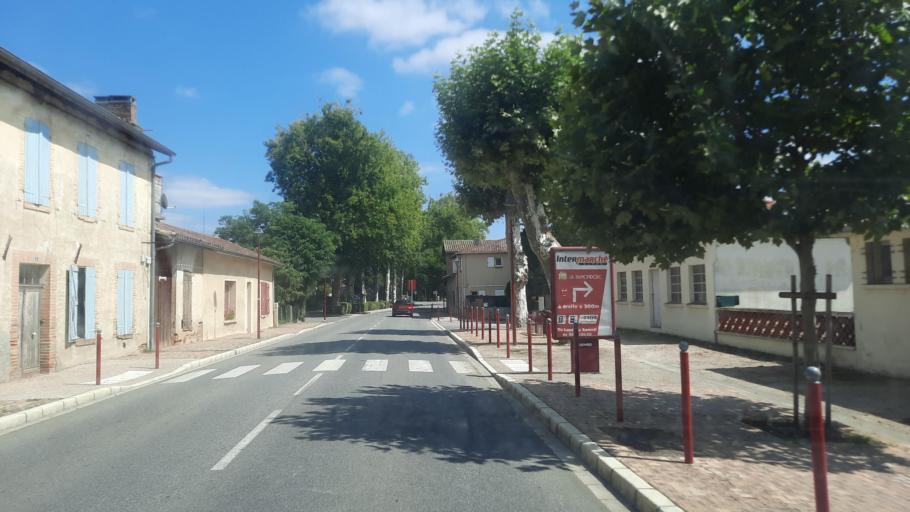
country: FR
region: Midi-Pyrenees
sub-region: Departement du Gers
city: Lombez
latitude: 43.4748
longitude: 0.9142
